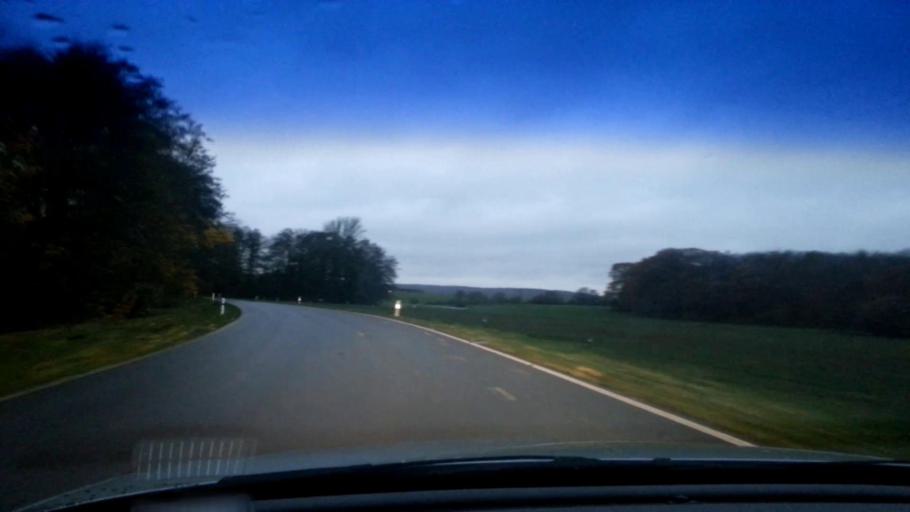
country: DE
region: Bavaria
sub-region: Upper Franconia
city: Schesslitz
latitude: 49.9534
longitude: 11.0280
